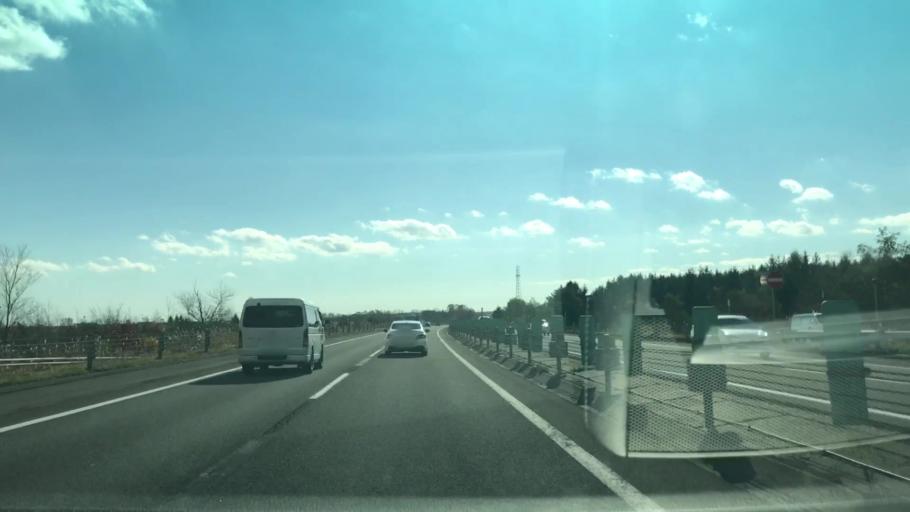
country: JP
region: Hokkaido
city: Kitahiroshima
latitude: 42.9056
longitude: 141.5507
